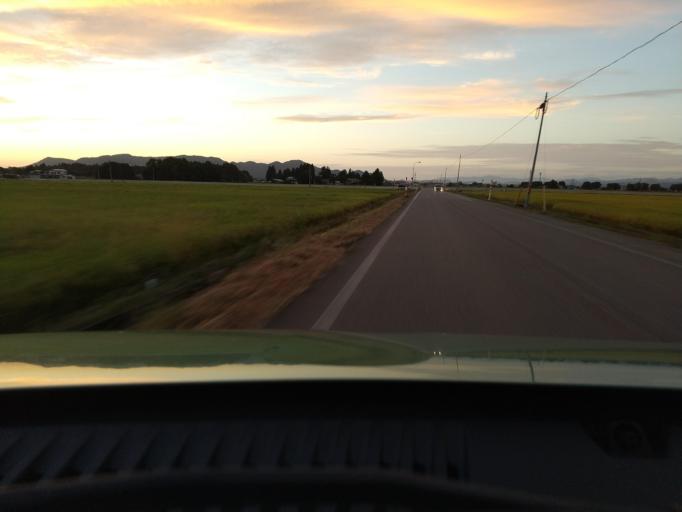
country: JP
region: Akita
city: Omagari
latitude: 39.4159
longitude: 140.4953
